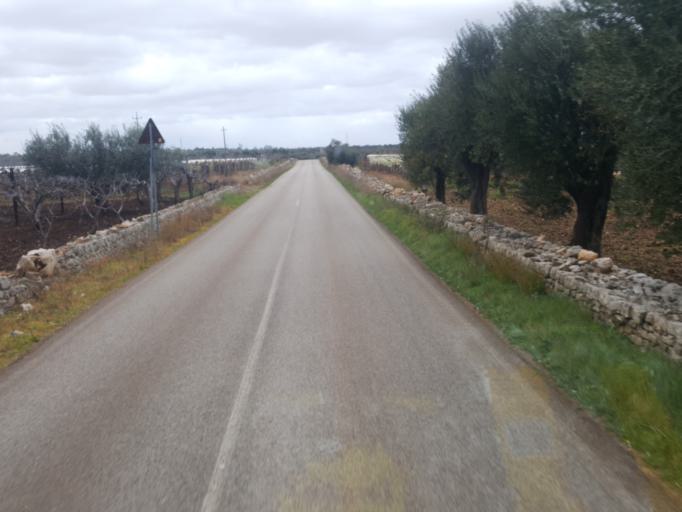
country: IT
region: Apulia
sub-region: Provincia di Bari
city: Turi
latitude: 40.9339
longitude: 17.0593
